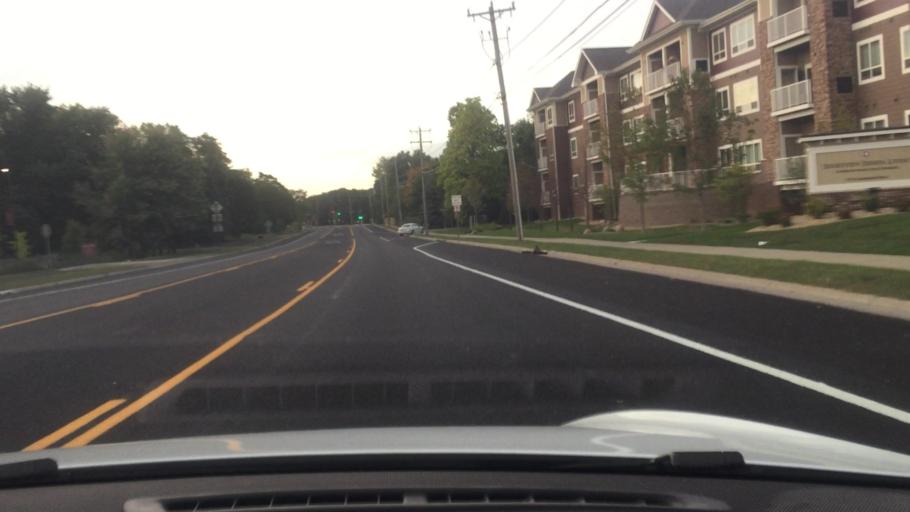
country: US
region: Minnesota
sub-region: Ramsey County
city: Shoreview
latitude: 45.0829
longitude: -93.1187
